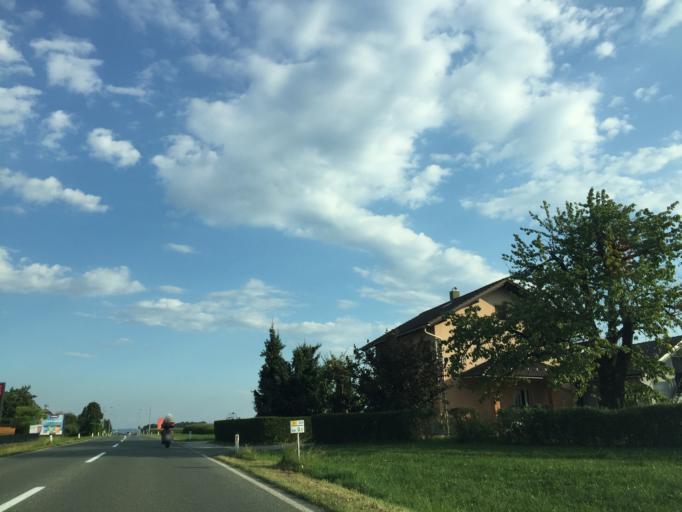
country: SI
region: Kranj
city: Kranj
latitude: 46.2225
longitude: 14.3583
